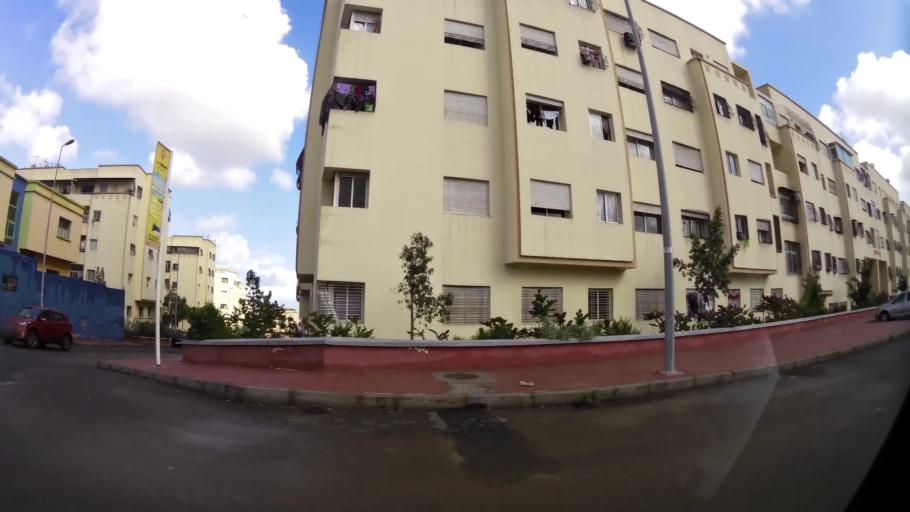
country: MA
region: Grand Casablanca
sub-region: Mediouna
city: Tit Mellil
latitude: 33.5769
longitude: -7.5292
